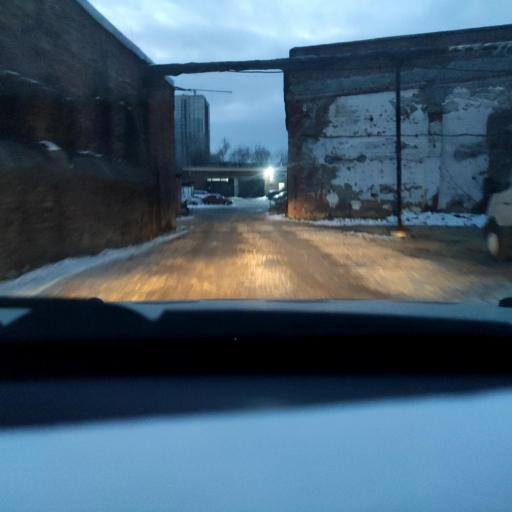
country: RU
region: Perm
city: Kondratovo
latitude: 57.9697
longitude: 56.1828
